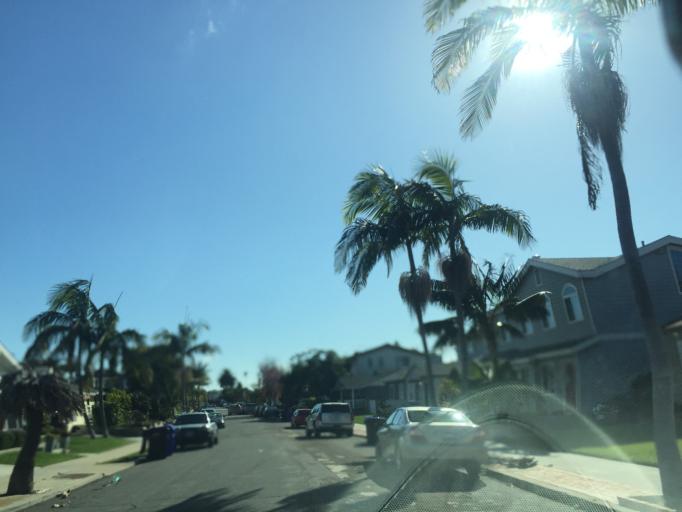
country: US
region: California
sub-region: San Diego County
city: La Jolla
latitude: 32.7840
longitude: -117.2387
